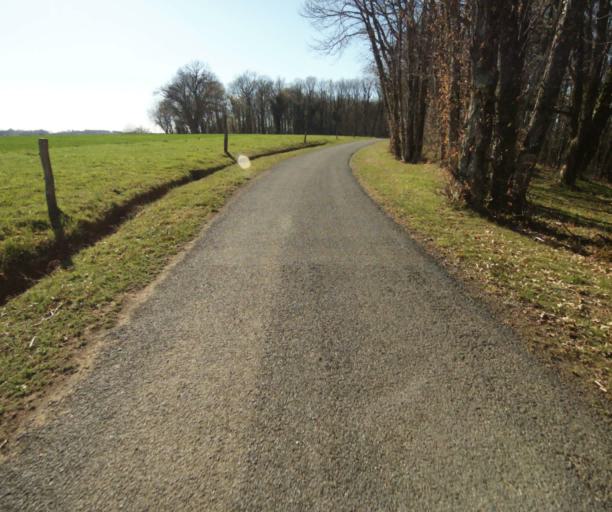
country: FR
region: Limousin
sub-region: Departement de la Correze
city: Chamboulive
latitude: 45.3966
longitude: 1.6754
